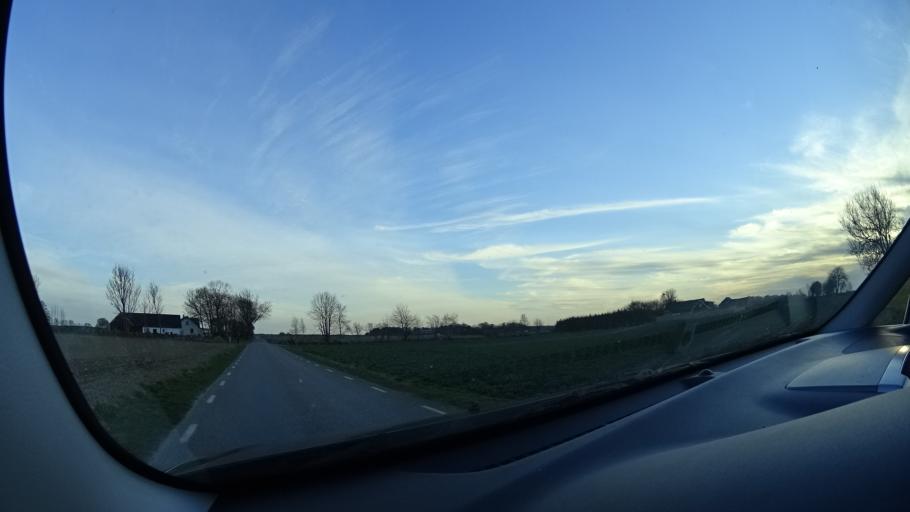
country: SE
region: Skane
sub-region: Eslovs Kommun
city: Stehag
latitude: 55.8589
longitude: 13.4439
